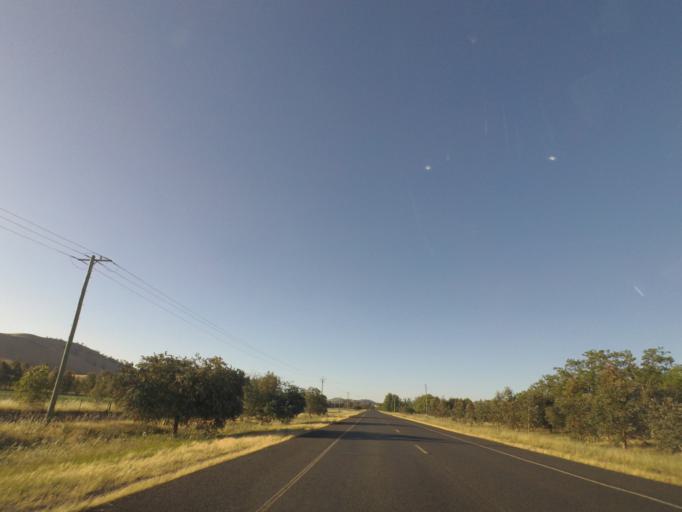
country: AU
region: New South Wales
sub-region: Gundagai
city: Gundagai
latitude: -34.9405
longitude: 148.1681
